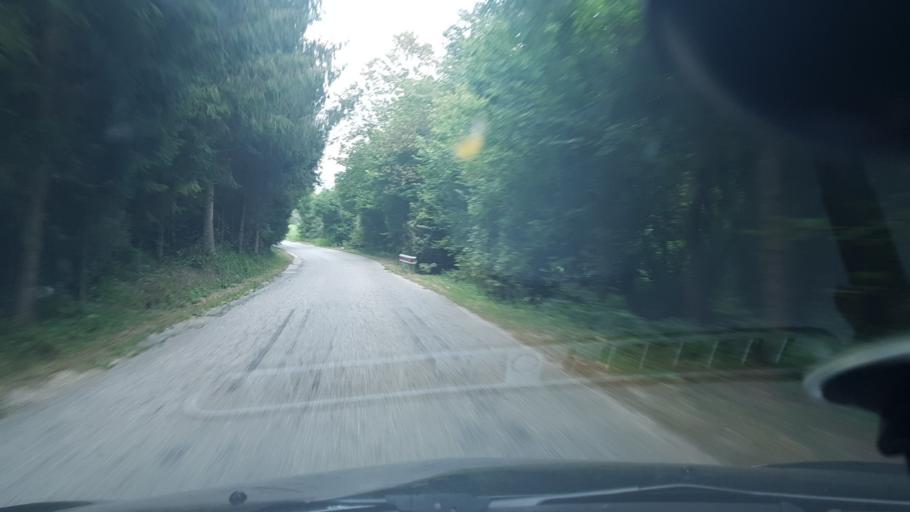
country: SI
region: Krsko
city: Senovo
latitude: 46.0177
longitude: 15.4991
